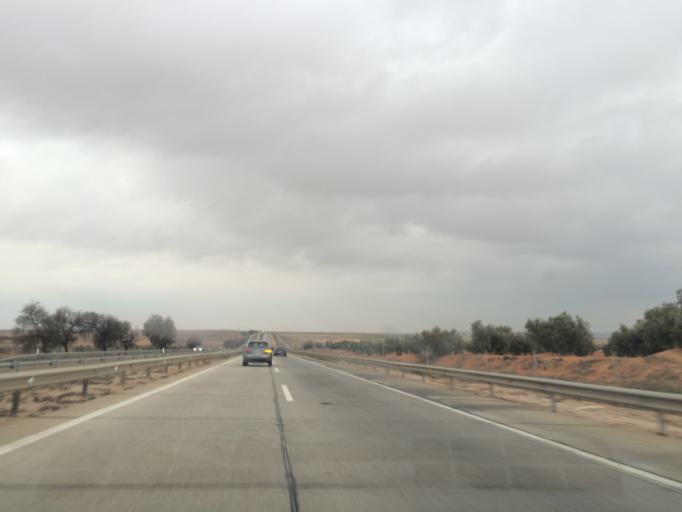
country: ES
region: Castille-La Mancha
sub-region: Province of Toledo
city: Madridejos
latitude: 39.5357
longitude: -3.5202
